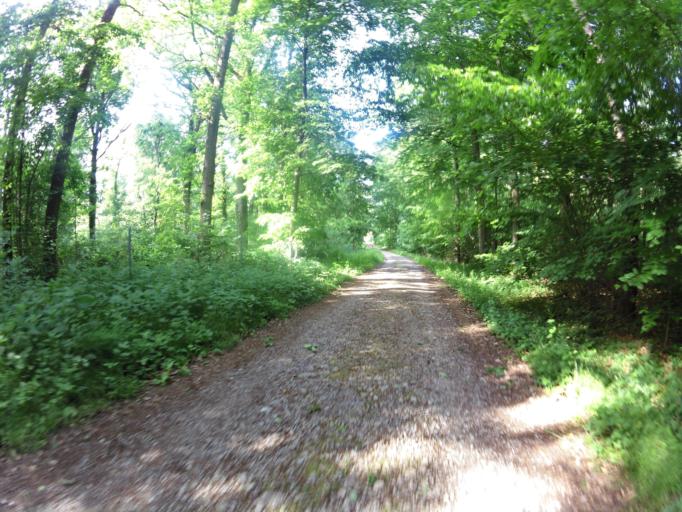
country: DE
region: Bavaria
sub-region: Regierungsbezirk Unterfranken
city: Ochsenfurt
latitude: 49.6890
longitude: 10.0651
